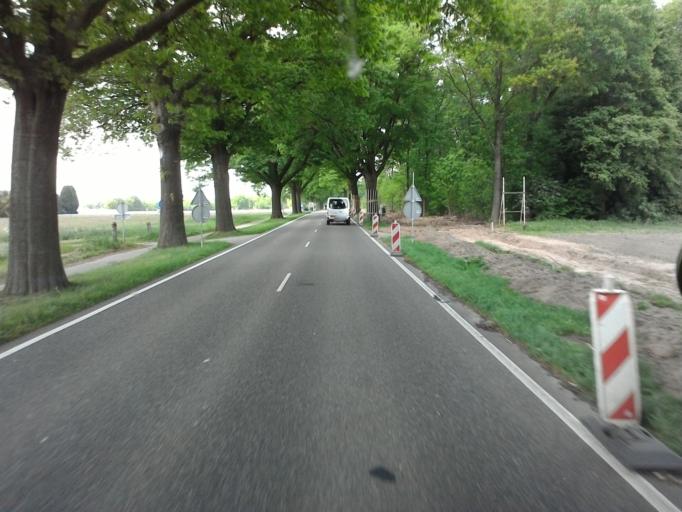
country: NL
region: North Brabant
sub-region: Gemeente Boxmeer
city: Boxmeer
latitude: 51.6497
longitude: 5.9951
